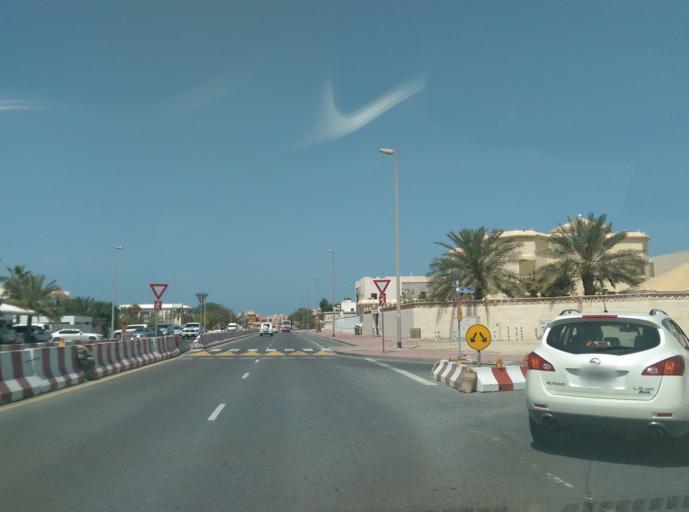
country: AE
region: Dubai
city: Dubai
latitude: 25.1869
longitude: 55.2380
